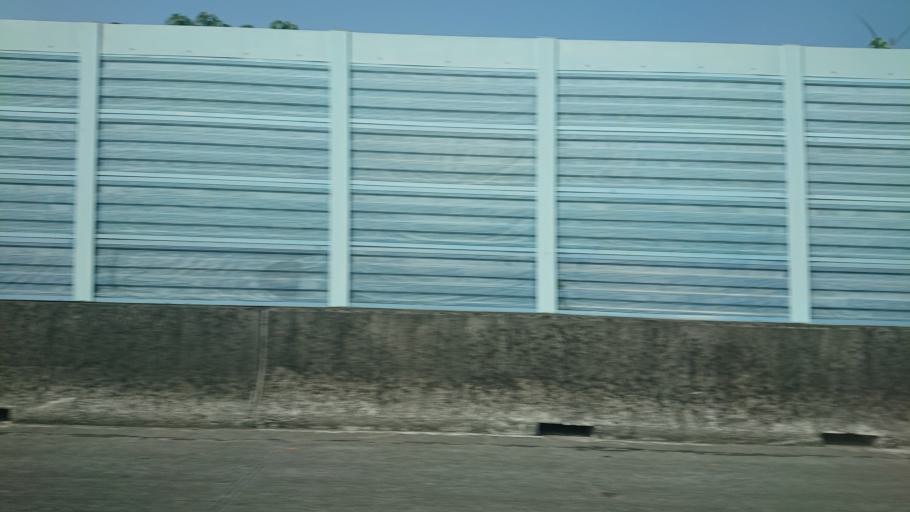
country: TW
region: Taiwan
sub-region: Nantou
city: Nantou
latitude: 23.8911
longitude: 120.7105
